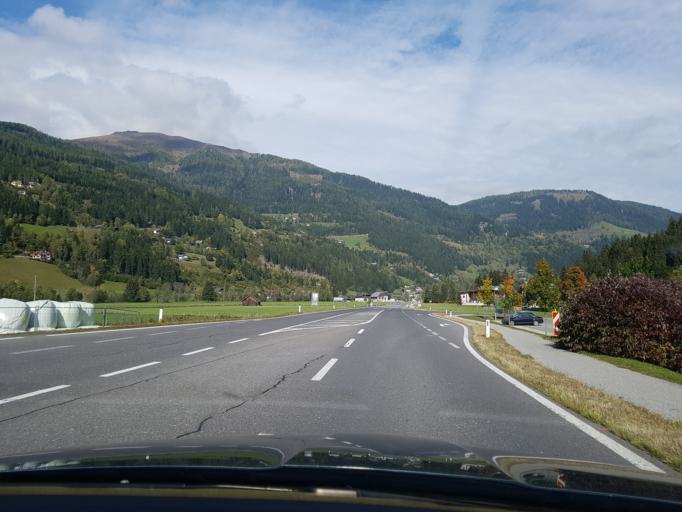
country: AT
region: Carinthia
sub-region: Politischer Bezirk Spittal an der Drau
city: Kleinkirchheim
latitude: 46.8175
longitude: 13.8632
